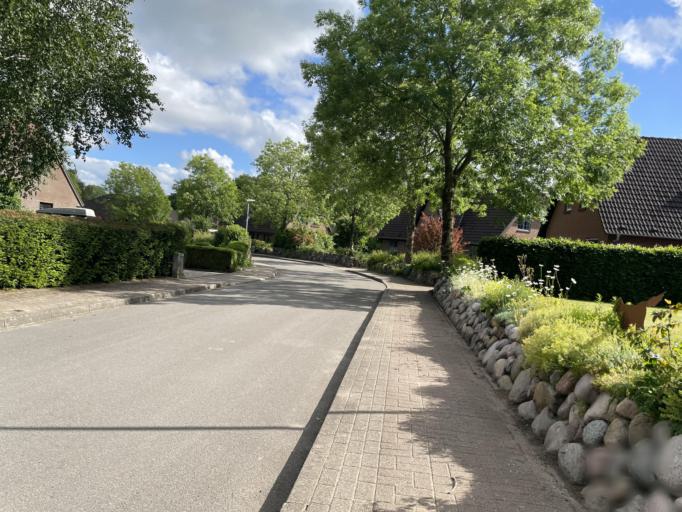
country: DE
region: Schleswig-Holstein
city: Mildstedt
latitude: 54.4662
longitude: 9.0984
